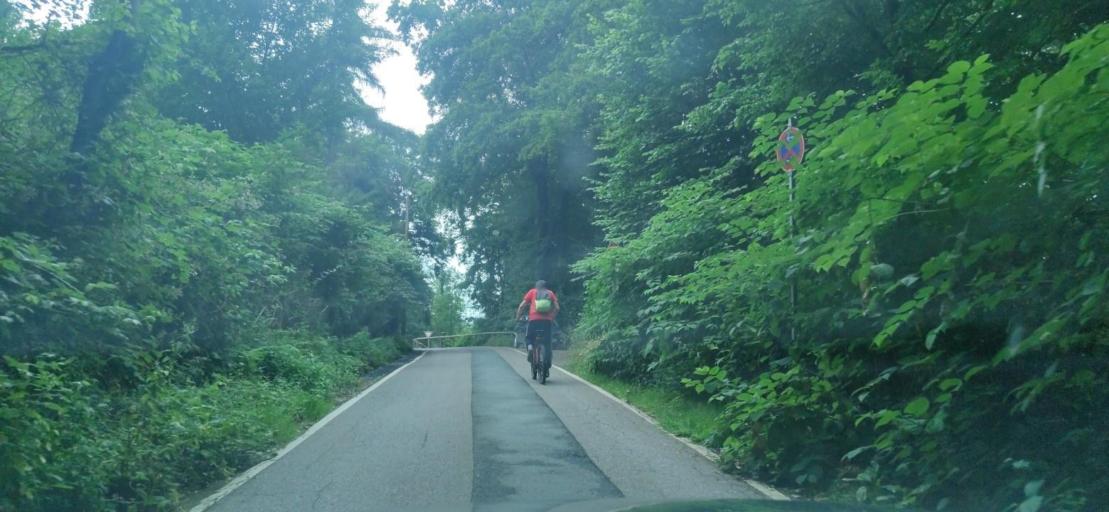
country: DE
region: North Rhine-Westphalia
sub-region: Regierungsbezirk Dusseldorf
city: Velbert
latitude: 51.3940
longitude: 7.0739
